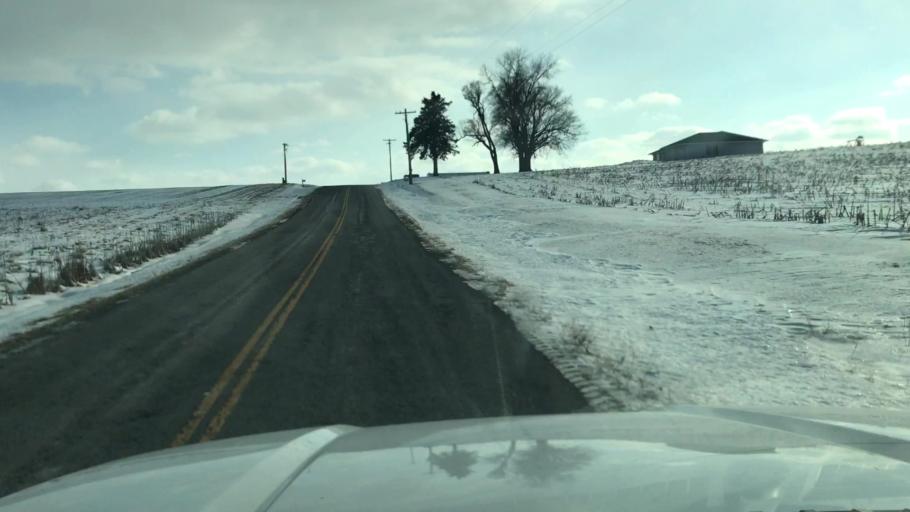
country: US
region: Missouri
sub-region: Nodaway County
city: Maryville
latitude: 40.1893
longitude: -95.0122
